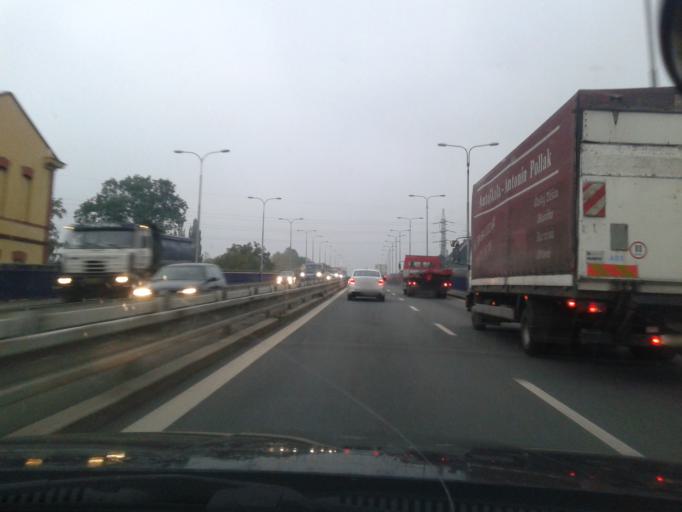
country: CZ
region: Moravskoslezsky
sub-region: Okres Ostrava-Mesto
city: Ostrava
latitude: 49.8050
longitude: 18.2641
